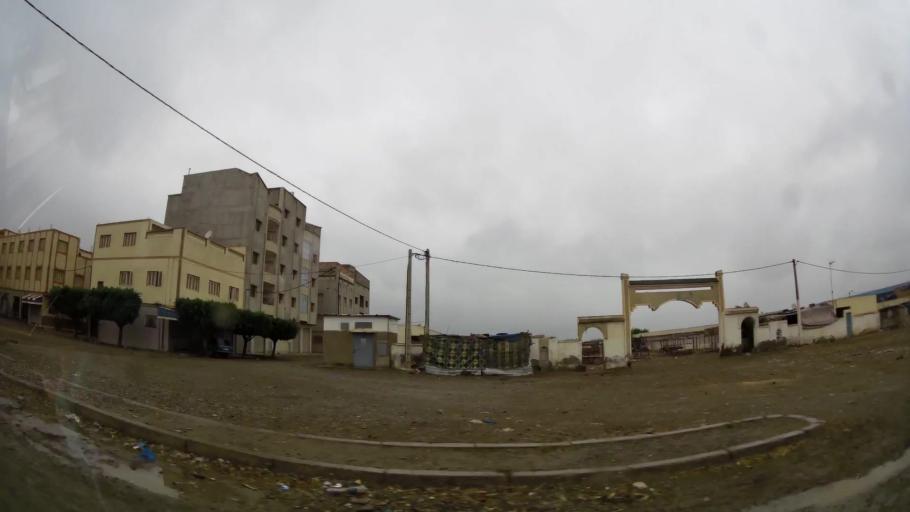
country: MA
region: Taza-Al Hoceima-Taounate
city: Imzourene
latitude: 35.1537
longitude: -3.8409
